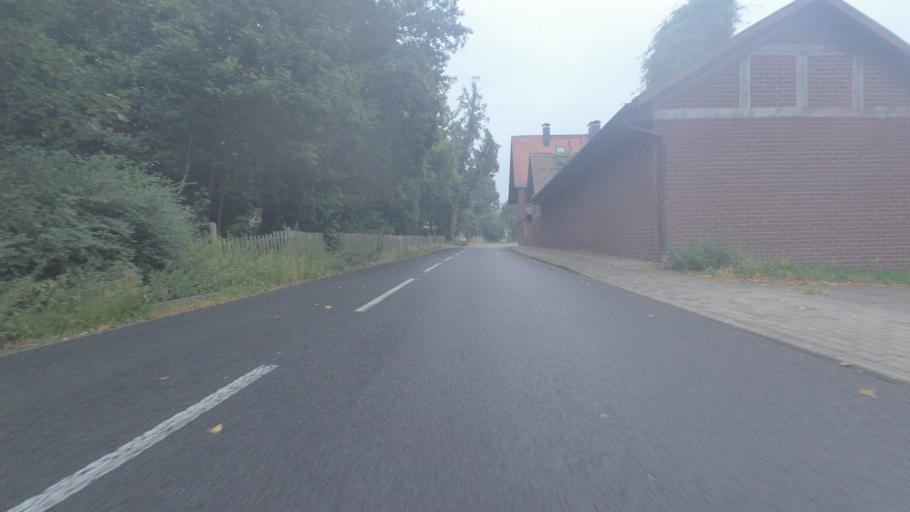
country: DE
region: Brandenburg
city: Heiligengrabe
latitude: 53.1419
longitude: 12.3487
